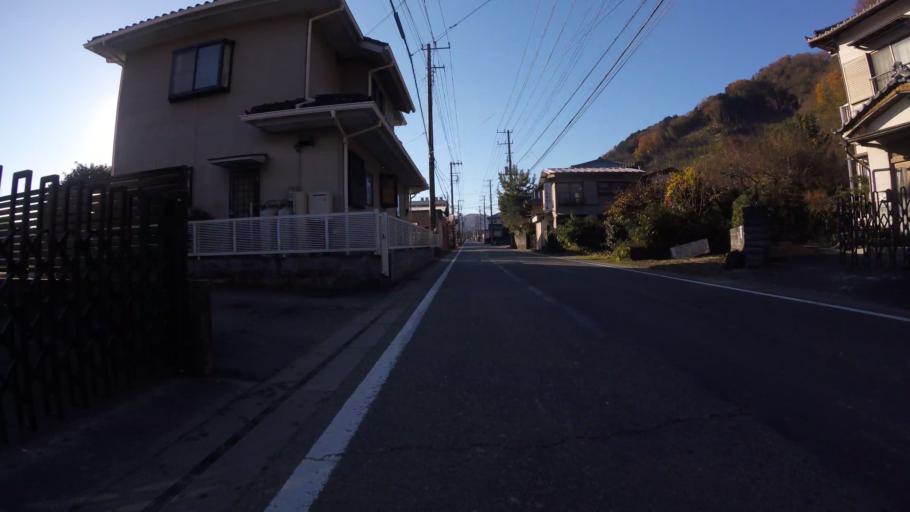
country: JP
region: Shizuoka
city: Ito
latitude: 34.9782
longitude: 138.9461
